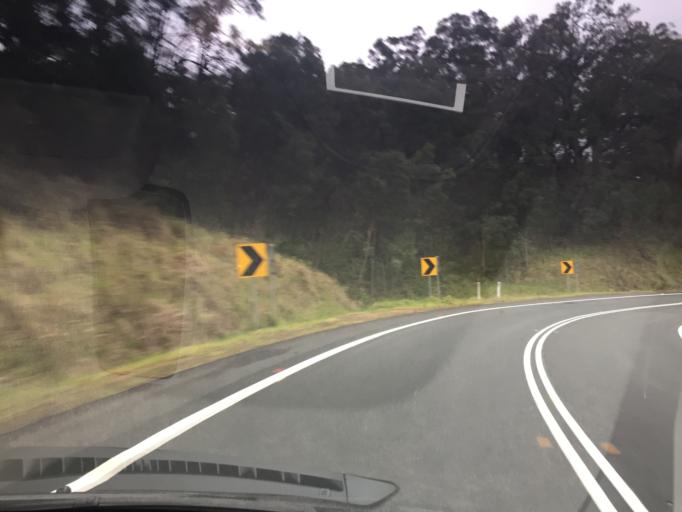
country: AU
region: New South Wales
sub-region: Bega Valley
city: Bega
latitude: -36.6127
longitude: 149.4939
